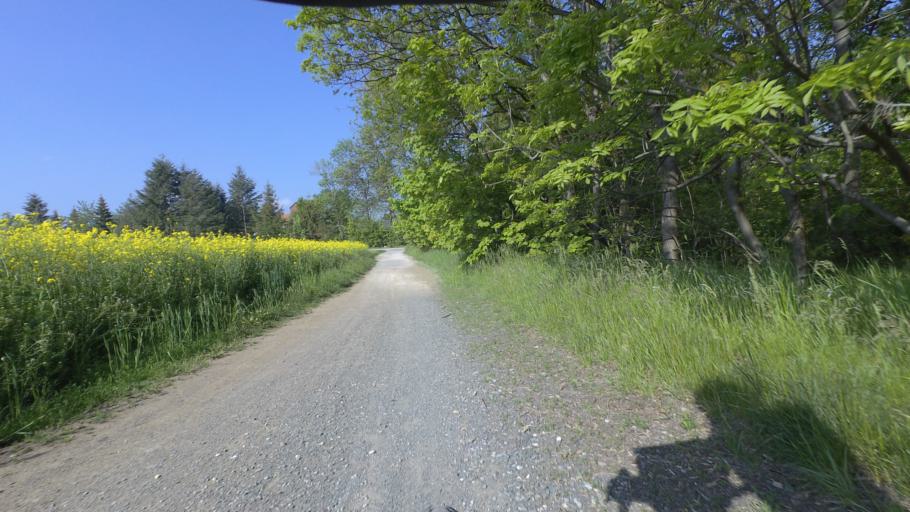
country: DE
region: Saxony-Anhalt
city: Wernigerode
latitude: 51.8616
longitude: 10.8172
